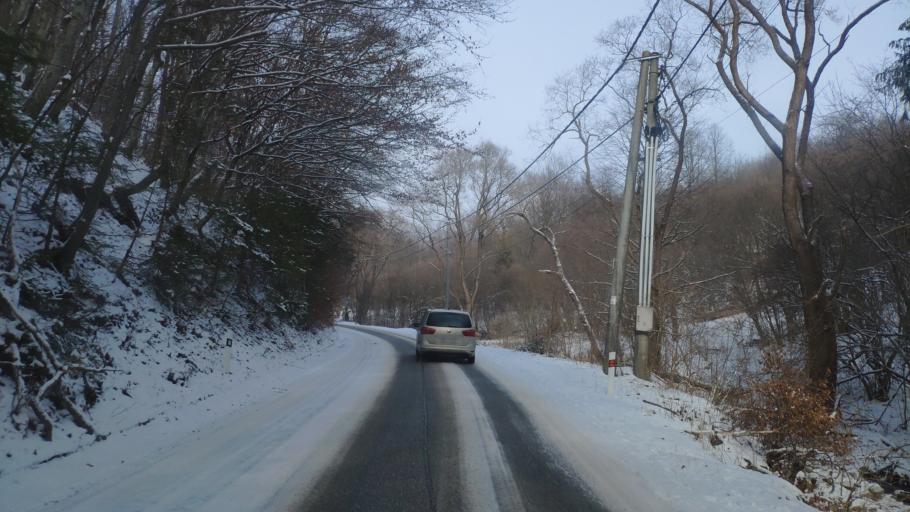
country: SK
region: Kosicky
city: Medzev
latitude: 48.7504
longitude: 21.0044
